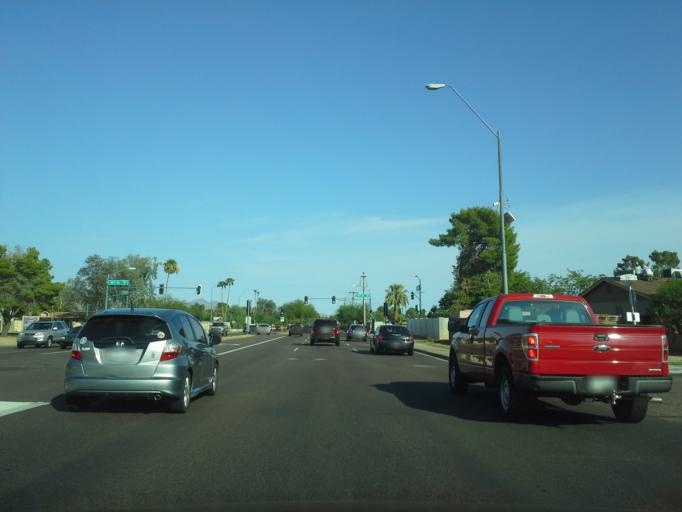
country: US
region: Arizona
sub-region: Maricopa County
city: Paradise Valley
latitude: 33.5970
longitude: -112.0056
